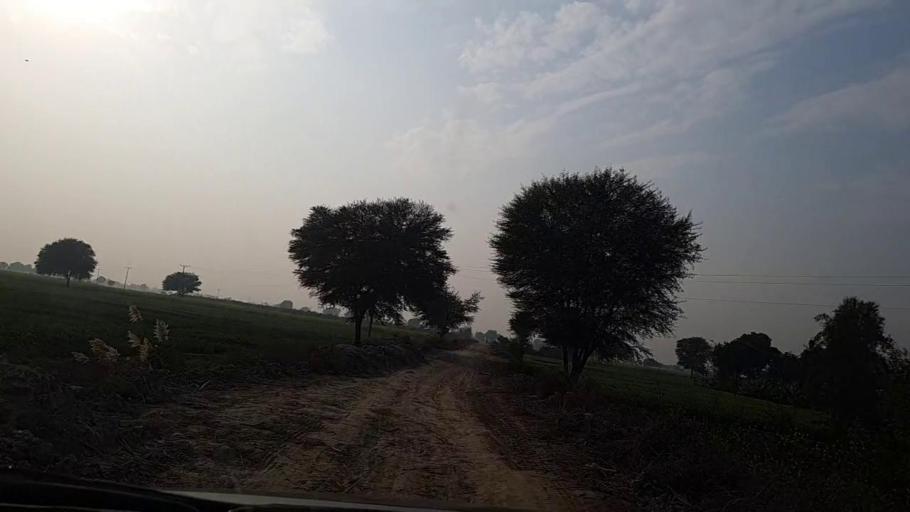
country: PK
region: Sindh
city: Nawabshah
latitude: 26.2695
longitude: 68.3209
